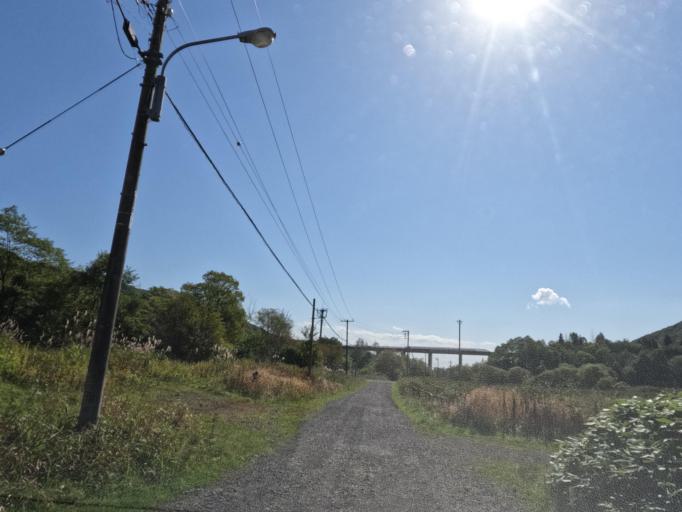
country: JP
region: Hokkaido
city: Muroran
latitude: 42.3908
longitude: 141.0310
